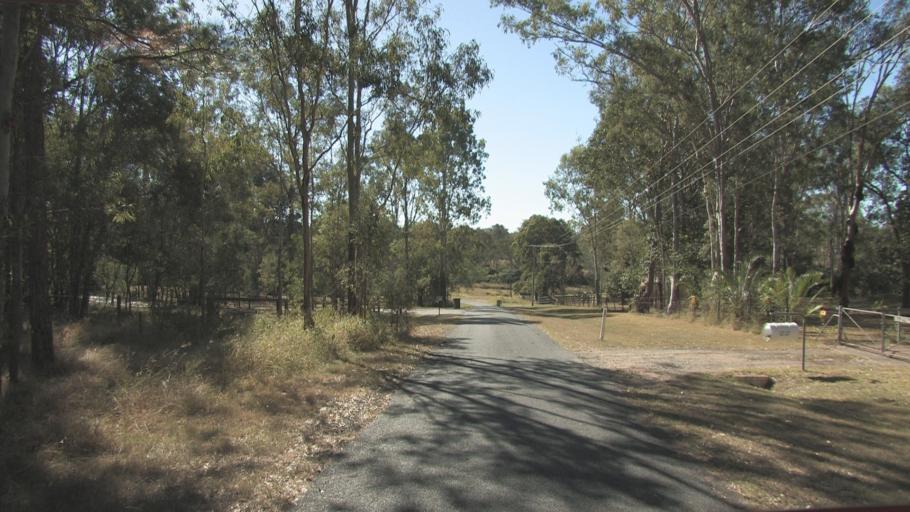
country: AU
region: Queensland
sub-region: Logan
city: North Maclean
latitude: -27.7662
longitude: 153.0295
